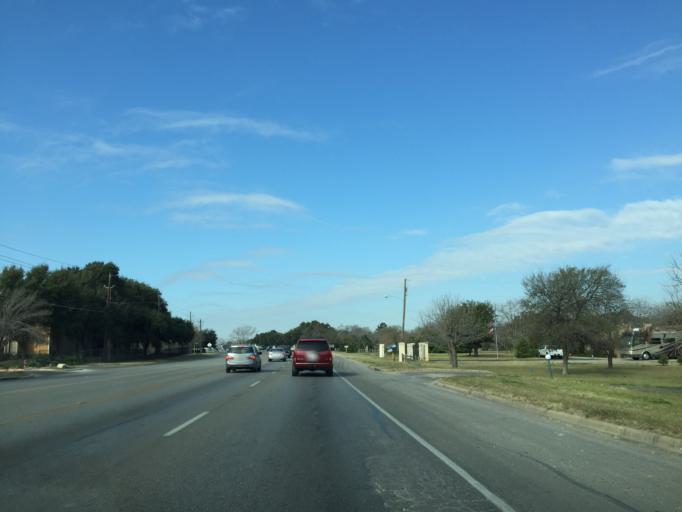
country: US
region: Texas
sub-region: Williamson County
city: Round Rock
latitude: 30.5189
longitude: -97.6743
